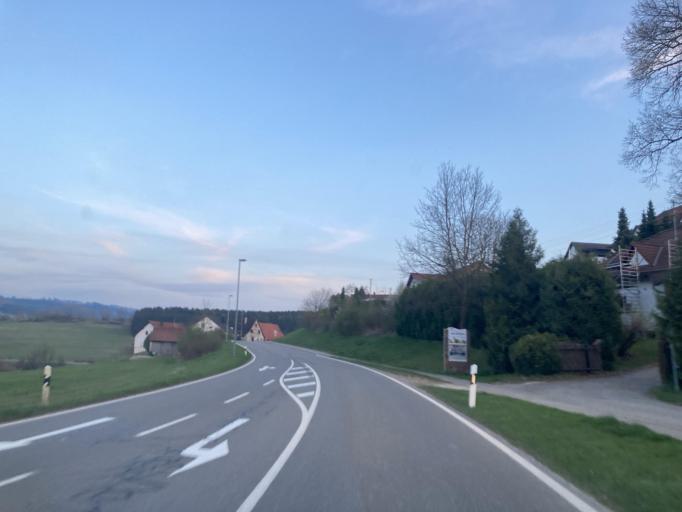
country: DE
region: Baden-Wuerttemberg
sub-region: Freiburg Region
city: Wellendingen
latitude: 48.1526
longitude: 8.7046
